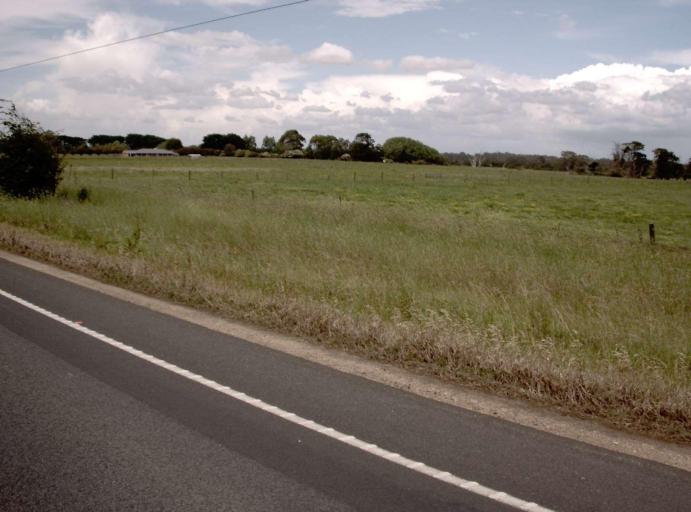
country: AU
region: Victoria
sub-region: Wellington
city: Sale
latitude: -38.0518
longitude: 147.0237
